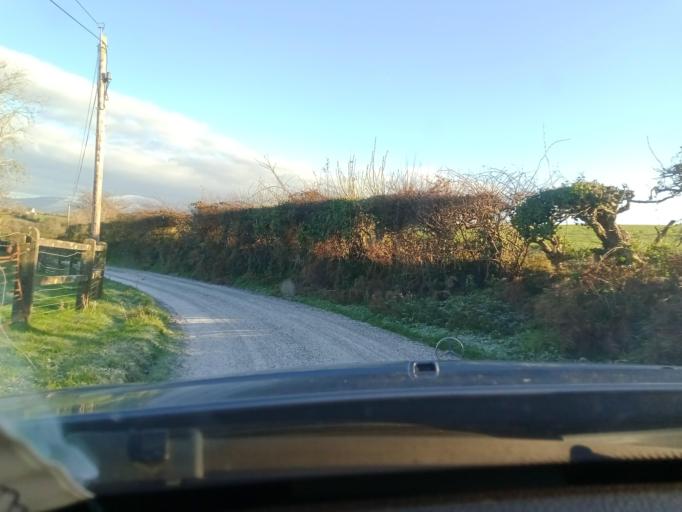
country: IE
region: Leinster
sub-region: Kilkenny
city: Graiguenamanagh
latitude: 52.5651
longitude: -6.9347
